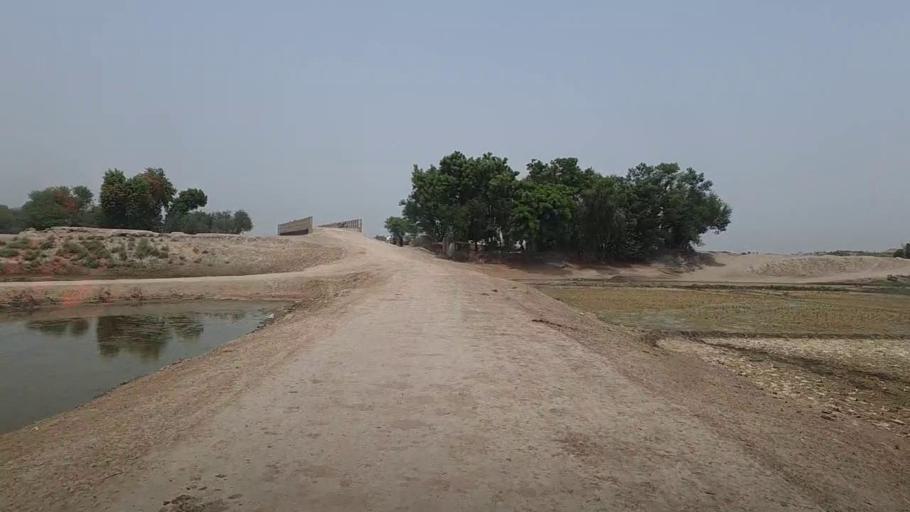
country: PK
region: Sindh
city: Sita Road
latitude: 27.0507
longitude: 67.8476
